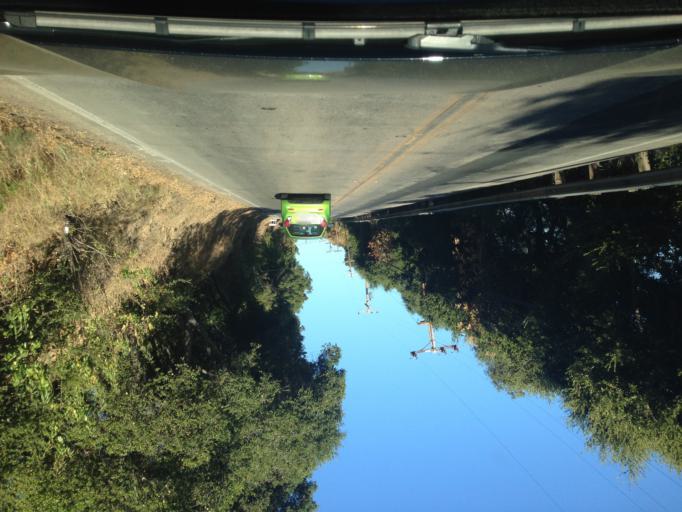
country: US
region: California
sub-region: Santa Clara County
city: Cambrian Park
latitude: 37.2361
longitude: -121.9421
